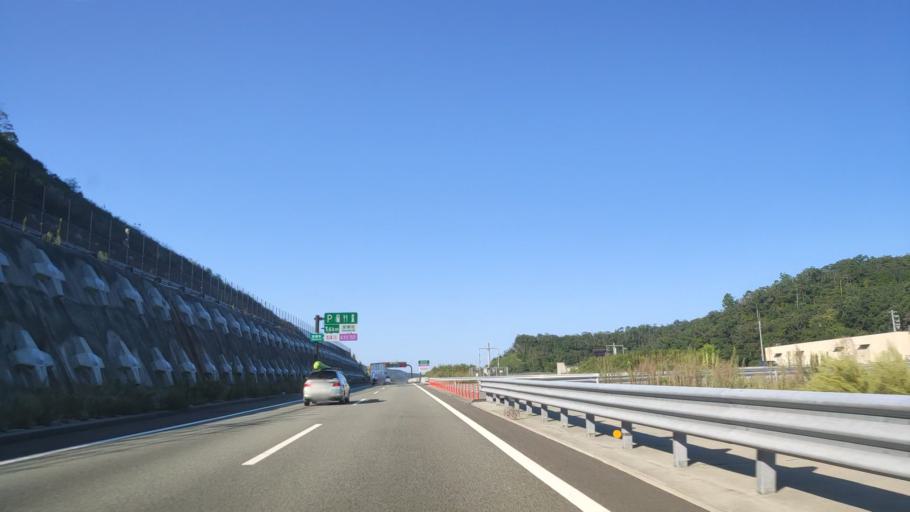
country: JP
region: Hyogo
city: Takarazuka
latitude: 34.8732
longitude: 135.3235
